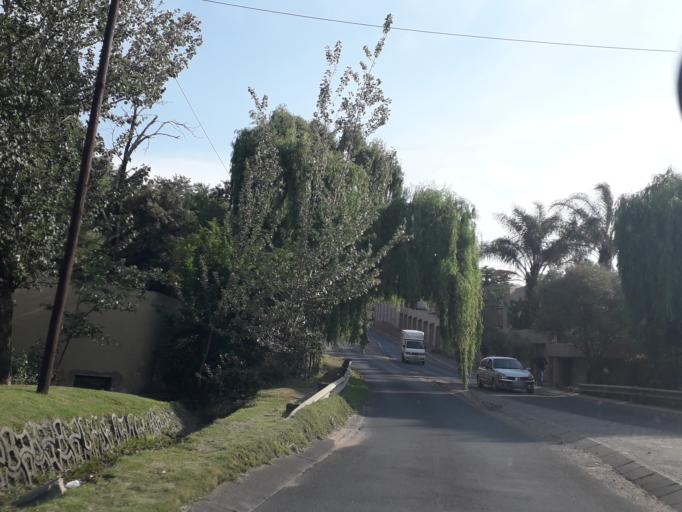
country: ZA
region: Gauteng
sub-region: City of Johannesburg Metropolitan Municipality
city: Johannesburg
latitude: -26.0890
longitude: 28.0415
